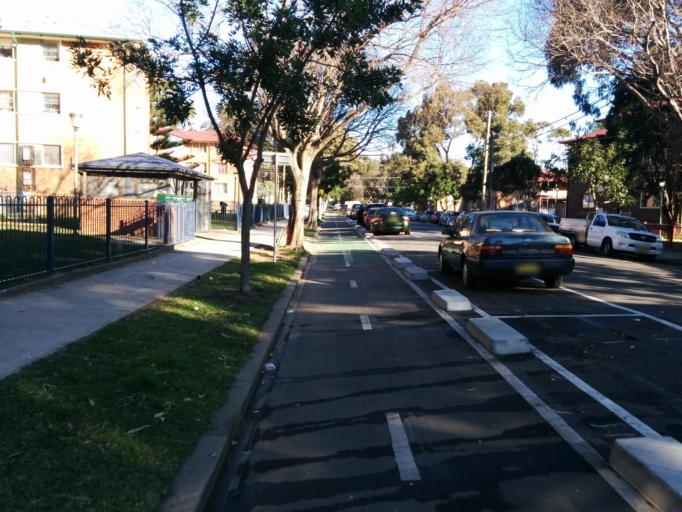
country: AU
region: New South Wales
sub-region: City of Sydney
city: Alexandria
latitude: -33.8988
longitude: 151.2025
